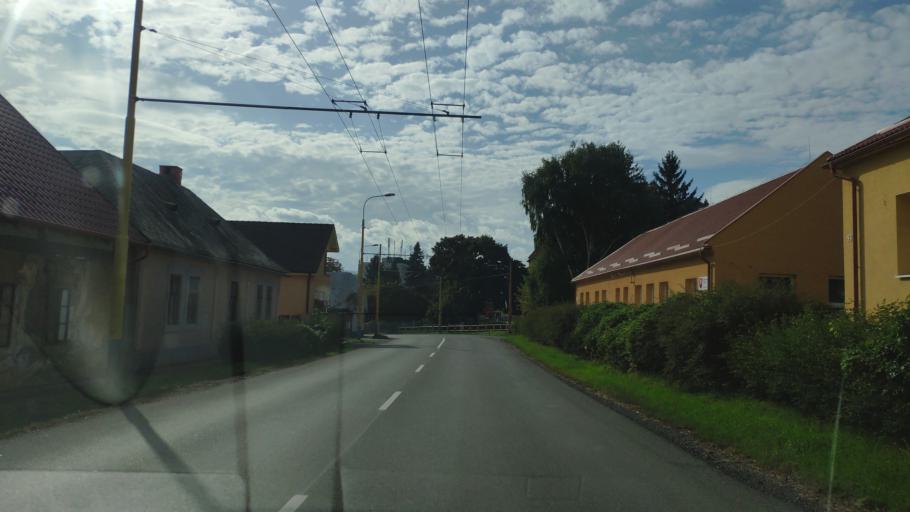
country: SK
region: Presovsky
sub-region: Okres Presov
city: Presov
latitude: 48.9787
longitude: 21.2710
